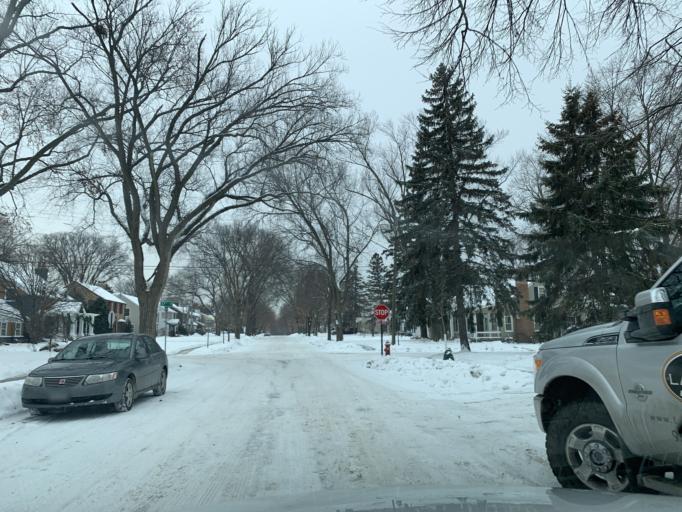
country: US
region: Minnesota
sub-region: Hennepin County
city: Saint Louis Park
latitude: 44.9363
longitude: -93.3316
